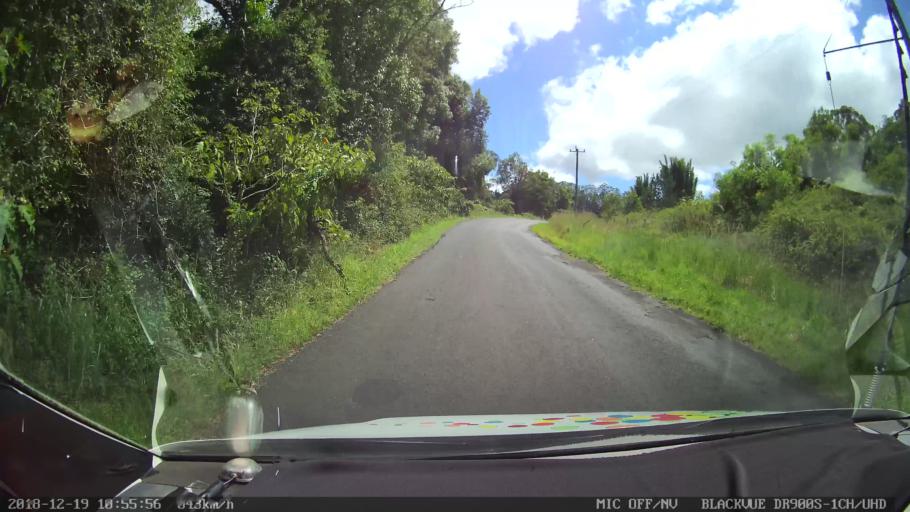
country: AU
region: New South Wales
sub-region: Lismore Municipality
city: Nimbin
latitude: -28.5960
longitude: 153.2579
